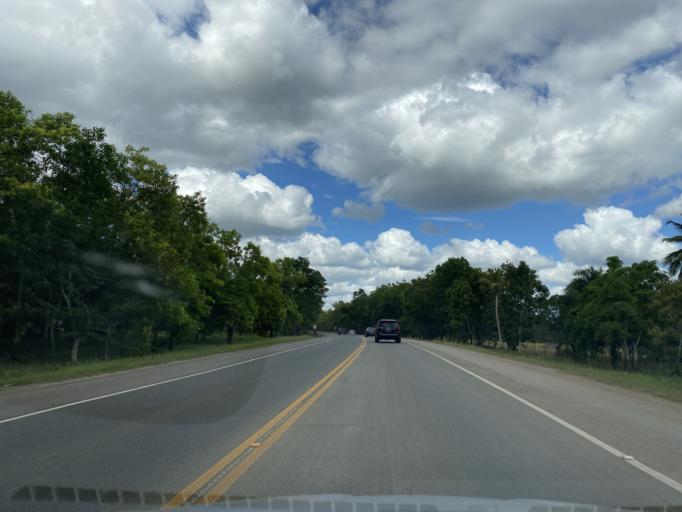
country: DO
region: Santo Domingo
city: Guerra
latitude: 18.6683
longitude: -69.7423
